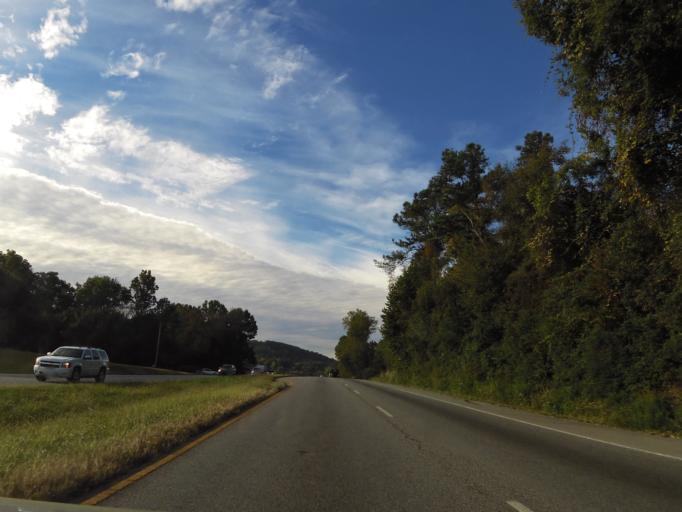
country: US
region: Tennessee
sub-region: Blount County
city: Eagleton Village
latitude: 35.8641
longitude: -83.9597
